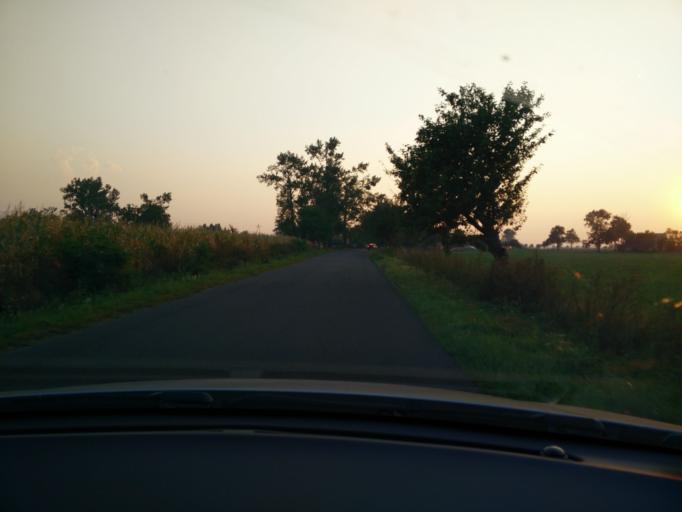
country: PL
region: Greater Poland Voivodeship
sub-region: Powiat wrzesinski
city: Miloslaw
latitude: 52.2429
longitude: 17.5242
